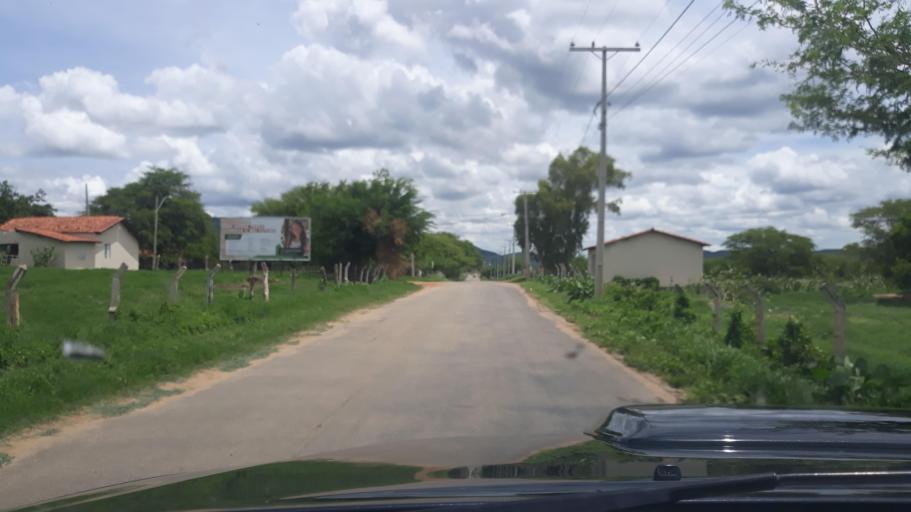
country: BR
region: Bahia
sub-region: Guanambi
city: Guanambi
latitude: -14.2951
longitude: -42.6968
